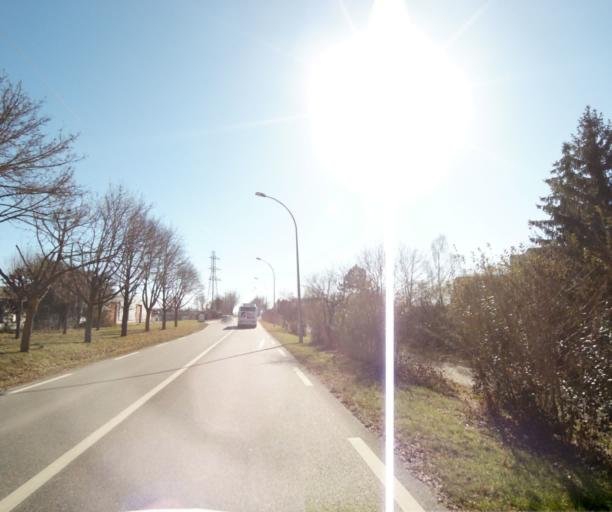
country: FR
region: Lorraine
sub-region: Departement de Meurthe-et-Moselle
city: Heillecourt
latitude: 48.6493
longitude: 6.2084
